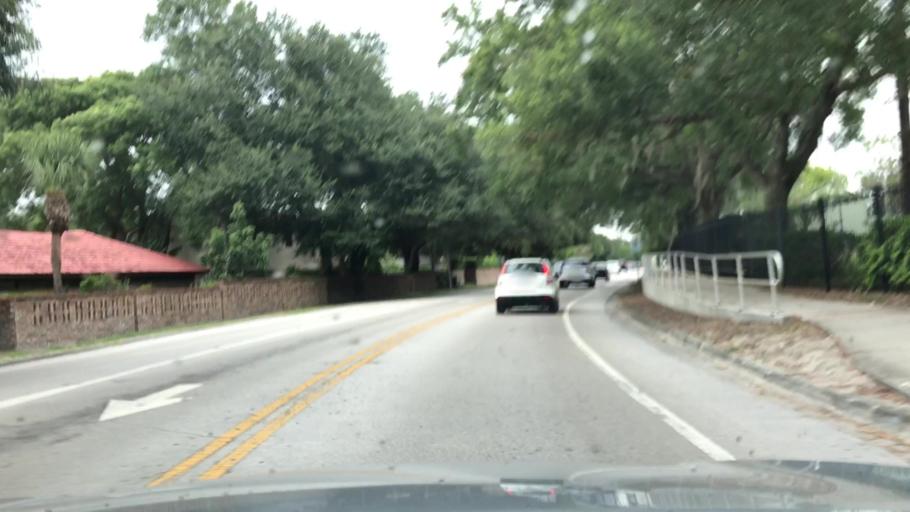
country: US
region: Florida
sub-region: Orange County
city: Winter Park
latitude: 28.5797
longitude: -81.3277
